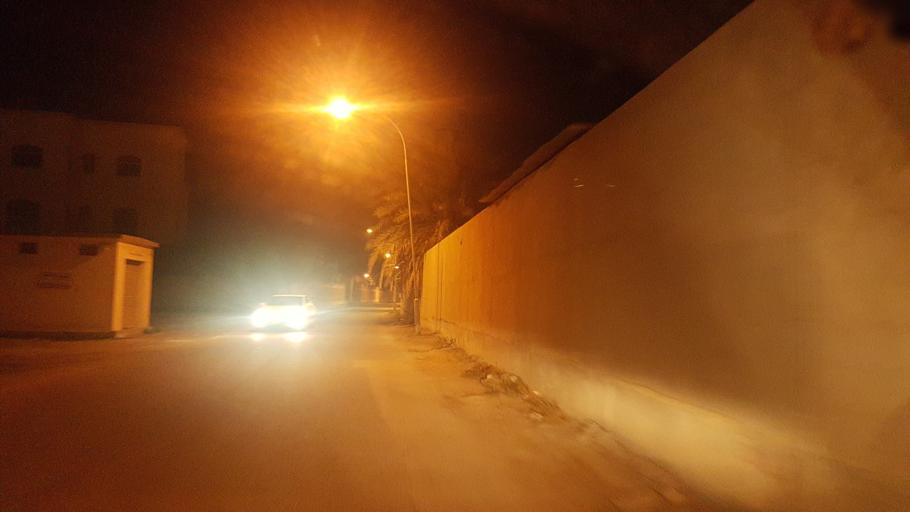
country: BH
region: Manama
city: Jidd Hafs
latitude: 26.2201
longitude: 50.4939
